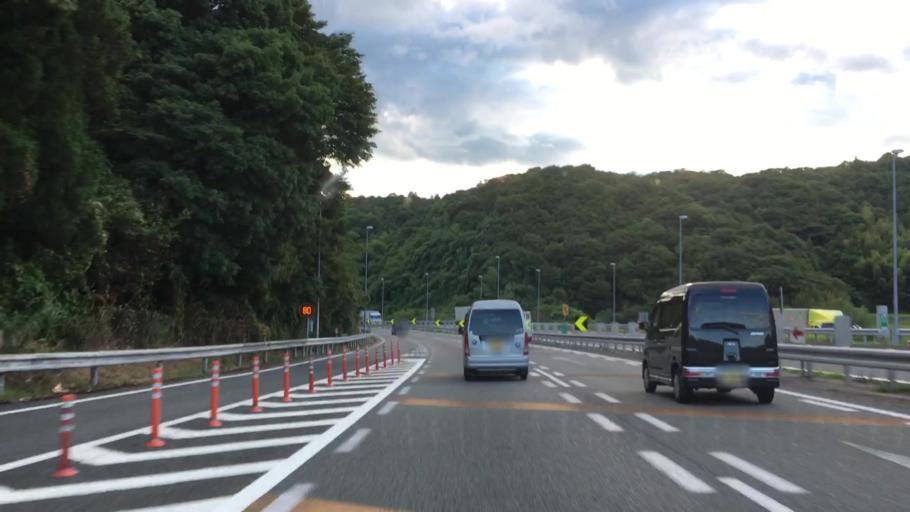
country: JP
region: Yamaguchi
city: Onoda
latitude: 34.1193
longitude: 131.2049
